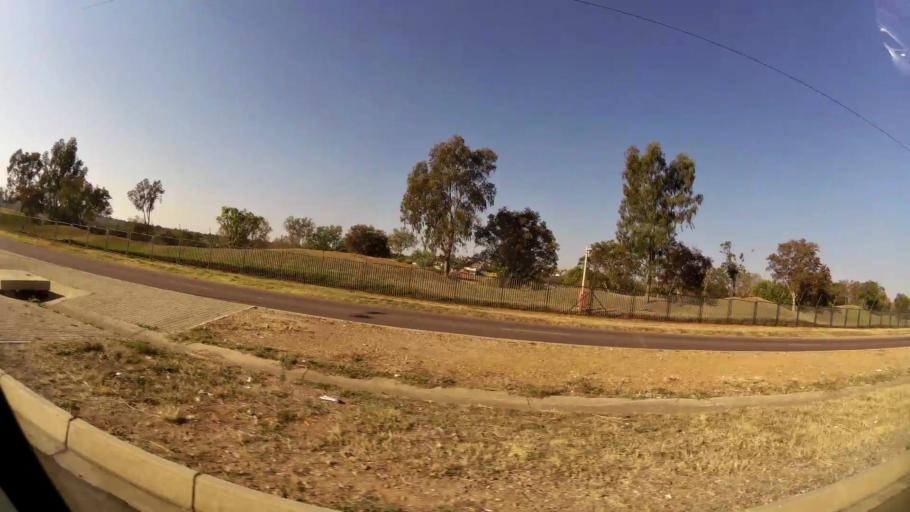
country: ZA
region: Gauteng
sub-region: City of Tshwane Metropolitan Municipality
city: Centurion
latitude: -25.8157
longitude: 28.3040
